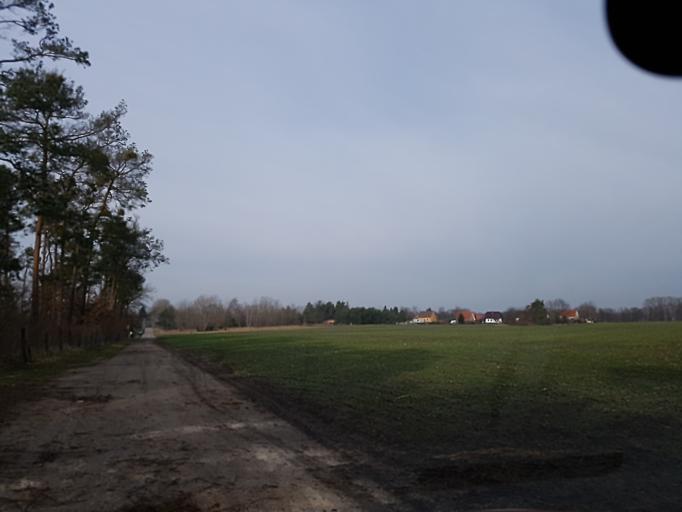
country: DE
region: Brandenburg
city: Ruckersdorf
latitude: 51.5903
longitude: 13.5529
